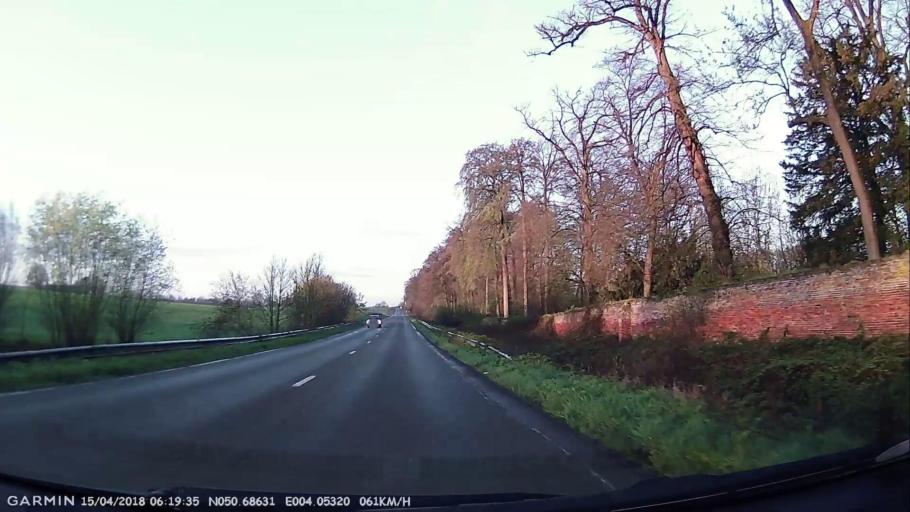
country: BE
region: Wallonia
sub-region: Province du Hainaut
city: Enghien
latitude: 50.6861
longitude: 4.0531
